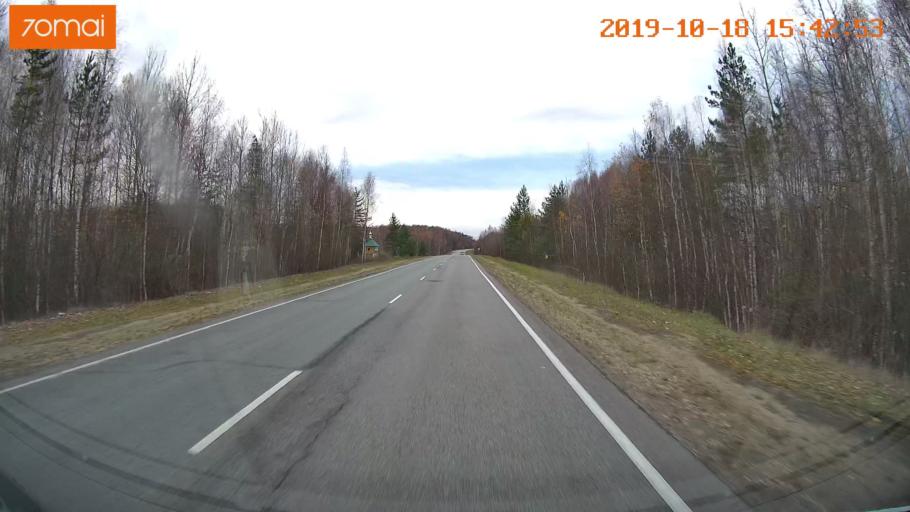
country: RU
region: Vladimir
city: Golovino
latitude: 55.9604
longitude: 40.5600
